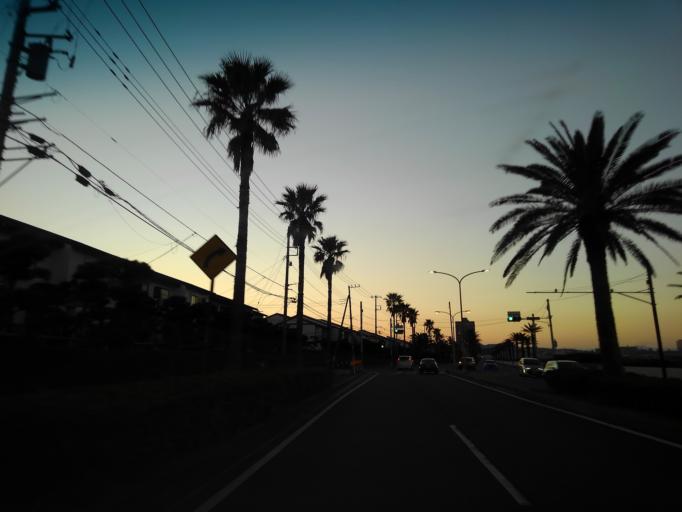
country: JP
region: Kanagawa
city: Yokosuka
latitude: 35.2636
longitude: 139.7037
